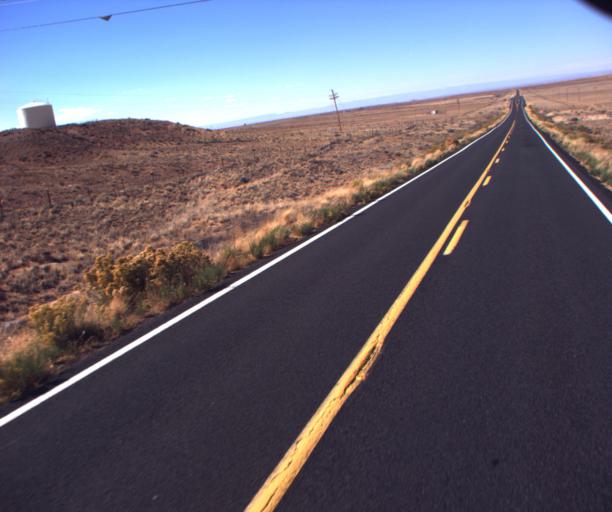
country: US
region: Arizona
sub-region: Coconino County
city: Tuba City
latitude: 35.9944
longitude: -111.0216
